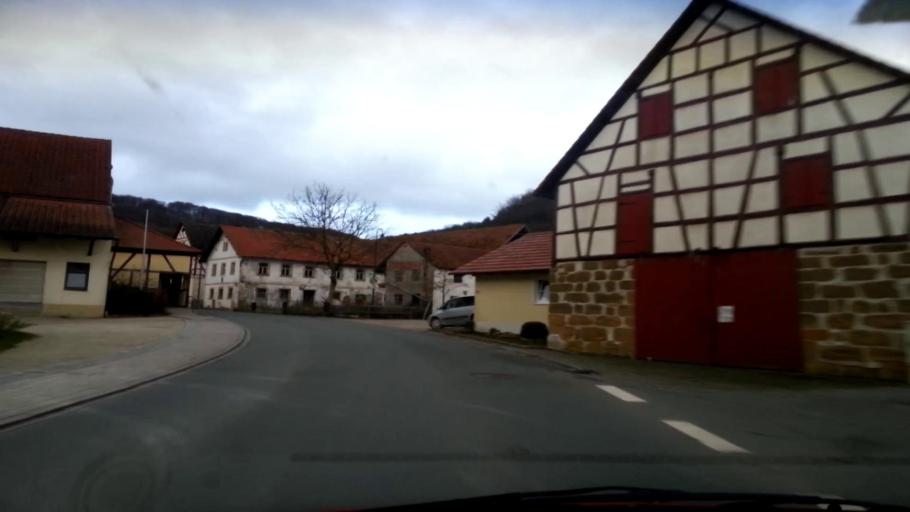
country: DE
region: Bavaria
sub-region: Upper Franconia
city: Poxdorf
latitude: 49.9186
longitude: 11.0729
